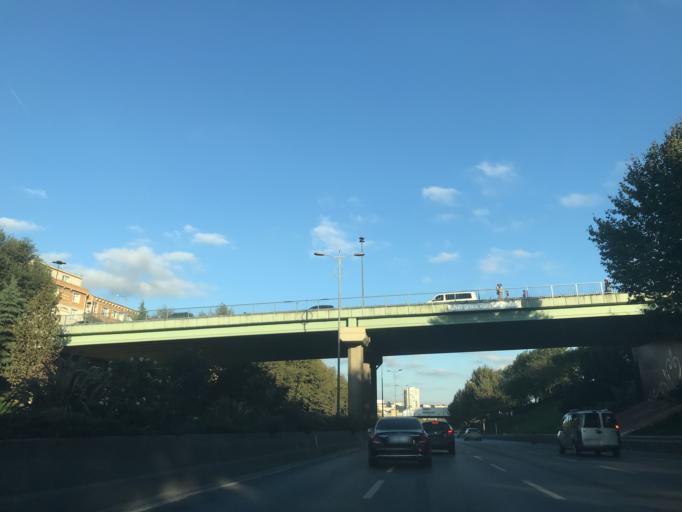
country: TR
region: Istanbul
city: Bagcilar
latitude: 41.0546
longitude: 28.8575
